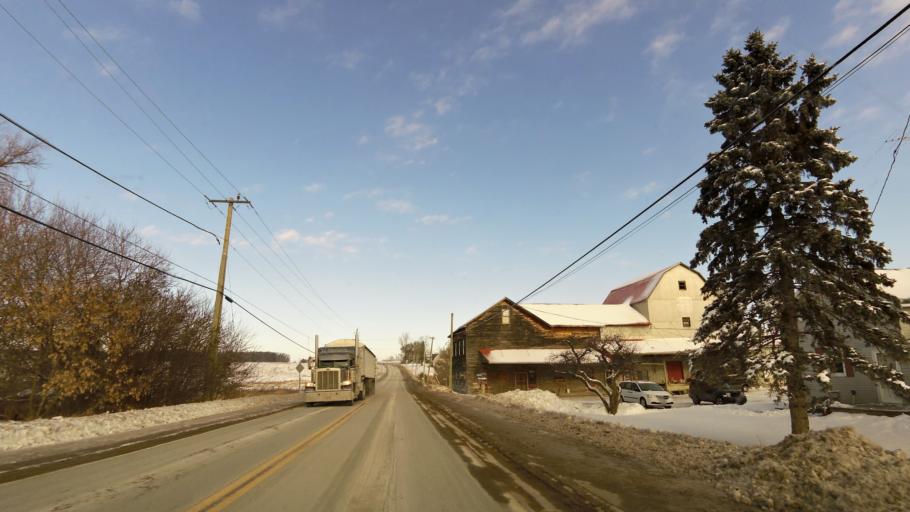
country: CA
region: Ontario
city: Quinte West
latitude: 44.1335
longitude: -77.7866
